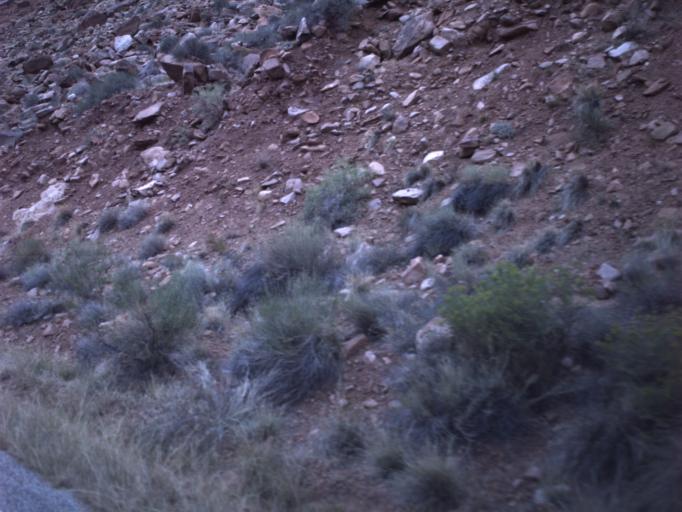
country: US
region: Utah
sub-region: Grand County
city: Moab
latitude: 38.7892
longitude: -109.3341
